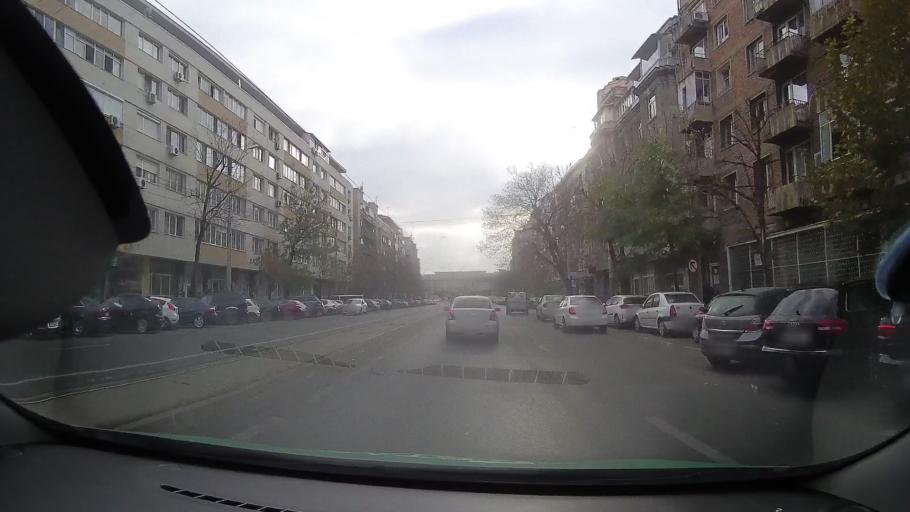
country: RO
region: Bucuresti
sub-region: Municipiul Bucuresti
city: Bucuresti
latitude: 44.4492
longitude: 26.0776
